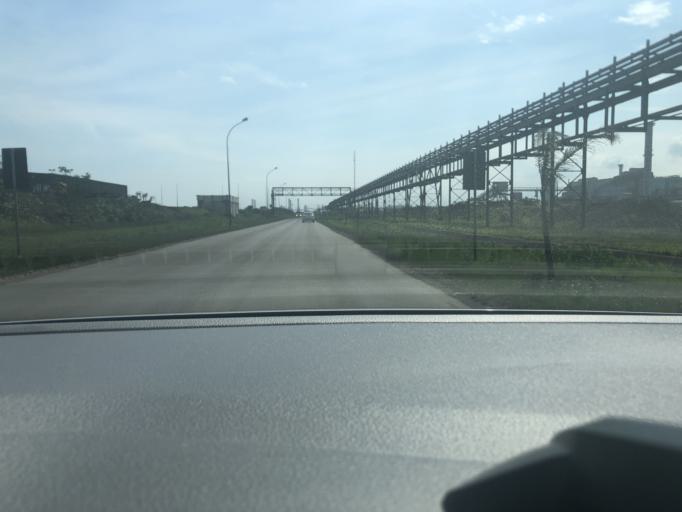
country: BR
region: Rio de Janeiro
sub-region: Itaguai
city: Itaguai
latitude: -22.9141
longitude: -43.7376
